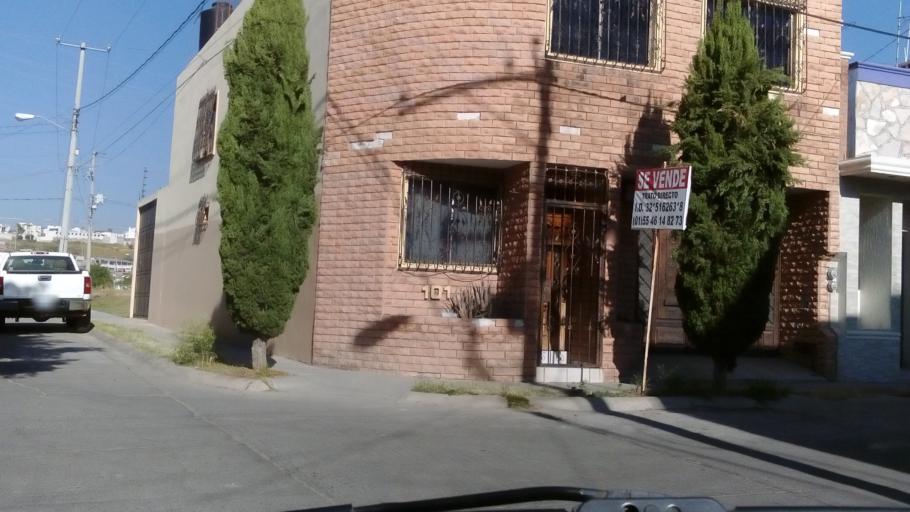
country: MX
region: Guanajuato
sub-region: Leon
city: Ejido la Joya
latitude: 21.1103
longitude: -101.7101
